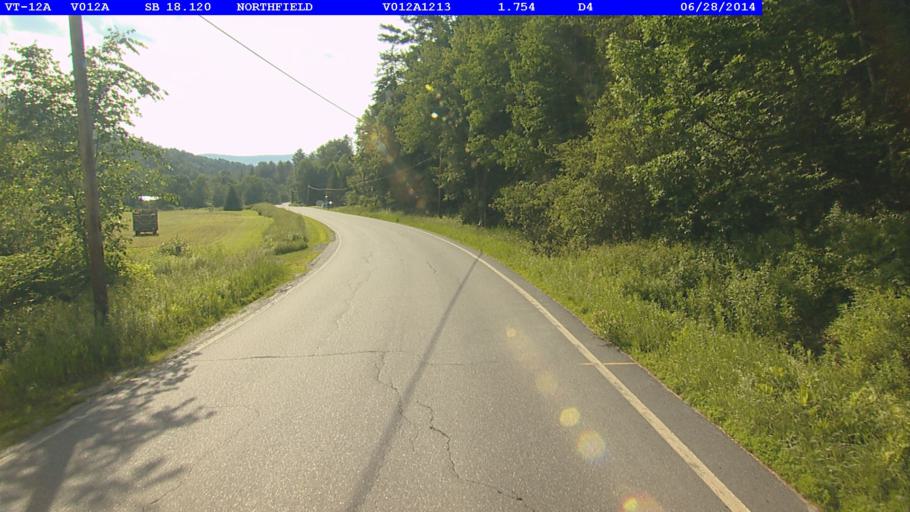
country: US
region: Vermont
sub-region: Washington County
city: Northfield
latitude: 44.1125
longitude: -72.6946
